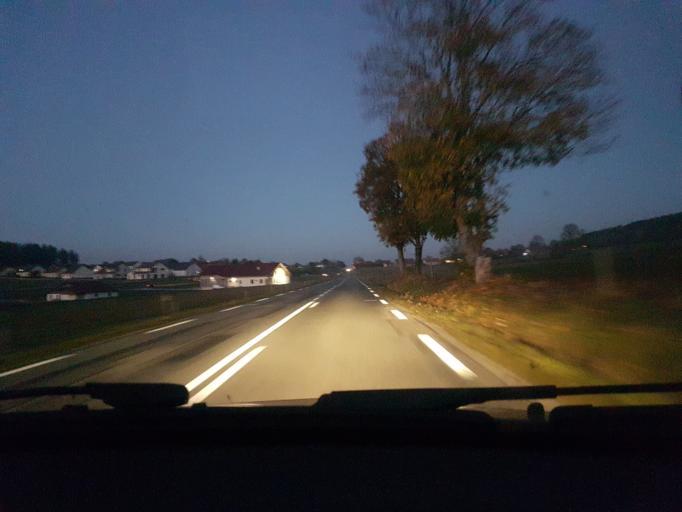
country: FR
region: Franche-Comte
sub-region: Departement du Doubs
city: Les Fins
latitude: 47.0973
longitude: 6.6539
